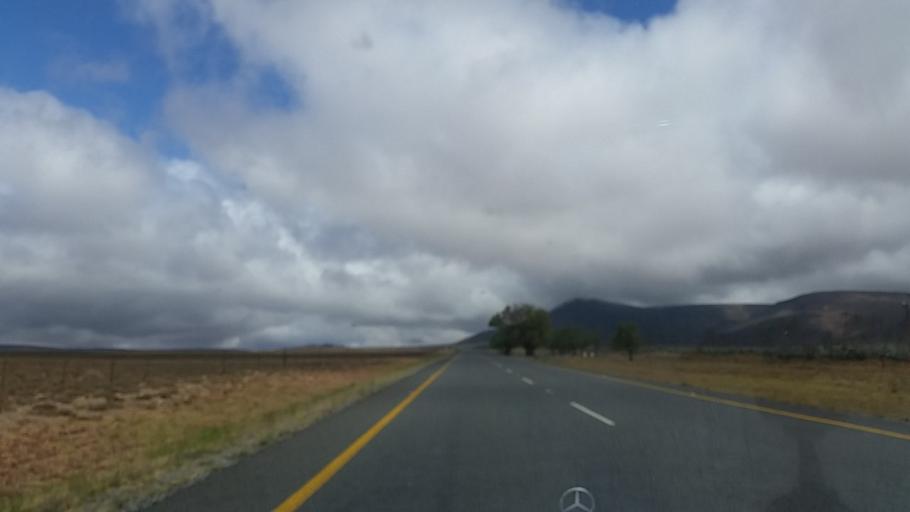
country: ZA
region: Eastern Cape
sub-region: Cacadu District Municipality
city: Graaff-Reinet
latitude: -32.0220
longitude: 24.6370
